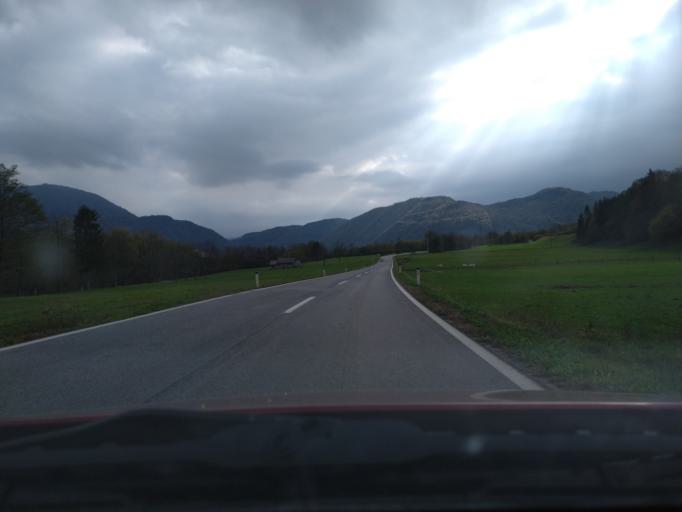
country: SI
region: Tolmin
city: Tolmin
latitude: 46.1889
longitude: 13.7040
